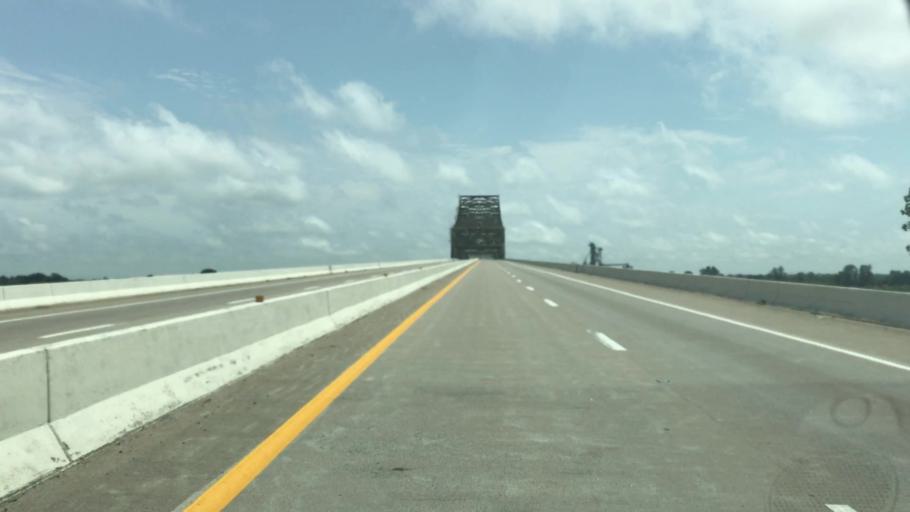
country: US
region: Missouri
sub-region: Pemiscot County
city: Caruthersville
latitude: 36.1188
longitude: -89.6153
